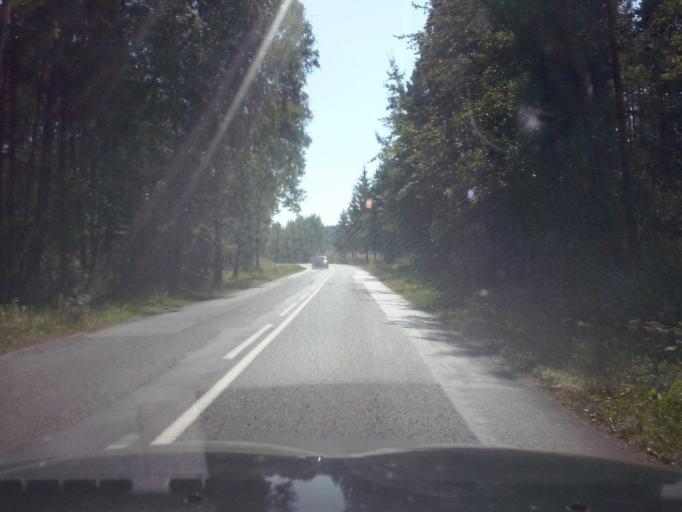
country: PL
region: Swietokrzyskie
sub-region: Powiat kielecki
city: Daleszyce
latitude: 50.8088
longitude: 20.7587
